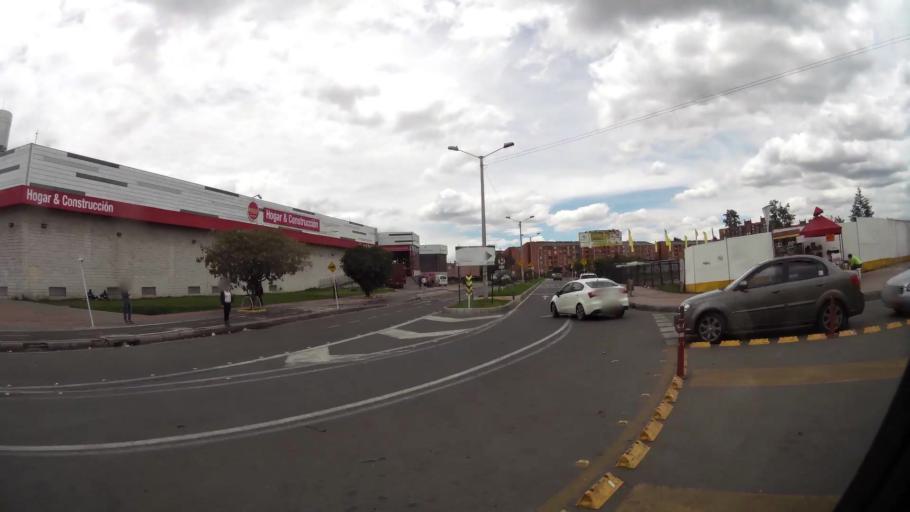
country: CO
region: Cundinamarca
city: Funza
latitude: 4.7225
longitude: -74.1234
